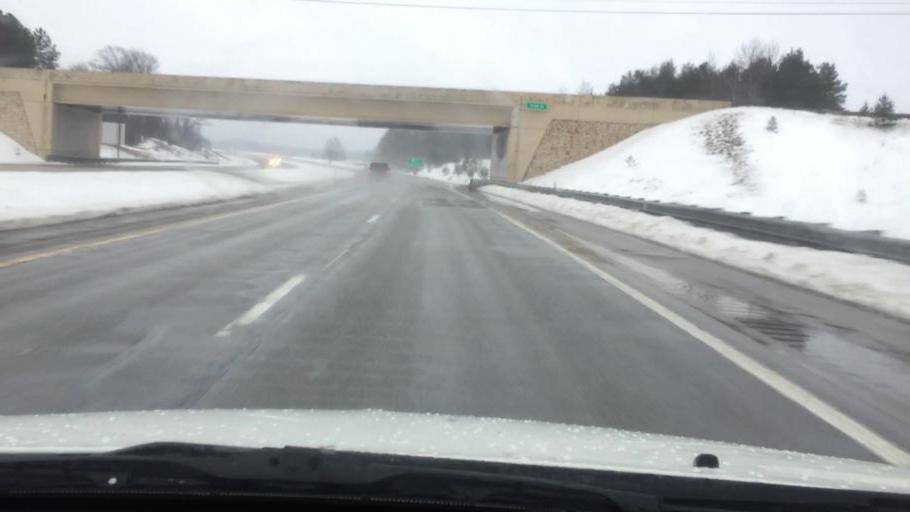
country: US
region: Michigan
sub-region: Wexford County
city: Cadillac
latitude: 44.2675
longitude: -85.3882
